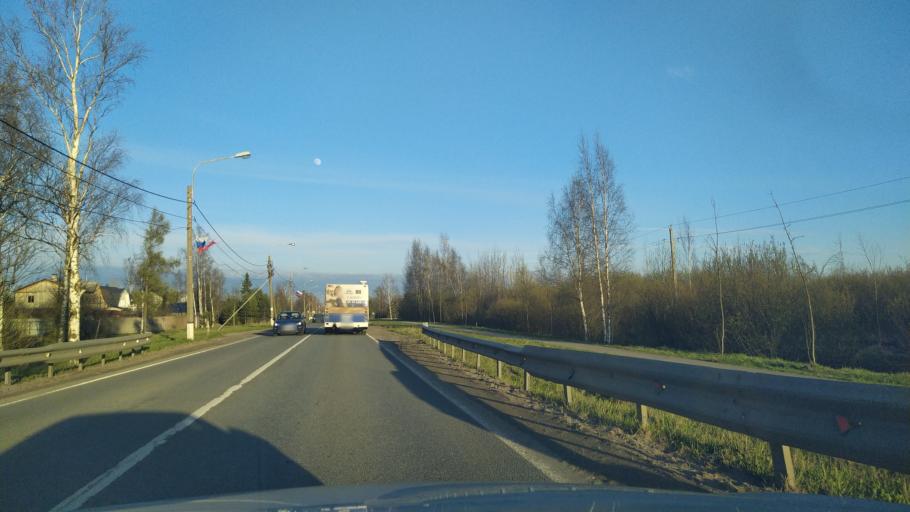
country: RU
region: St.-Petersburg
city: Aleksandrovskaya
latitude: 59.7374
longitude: 30.3295
